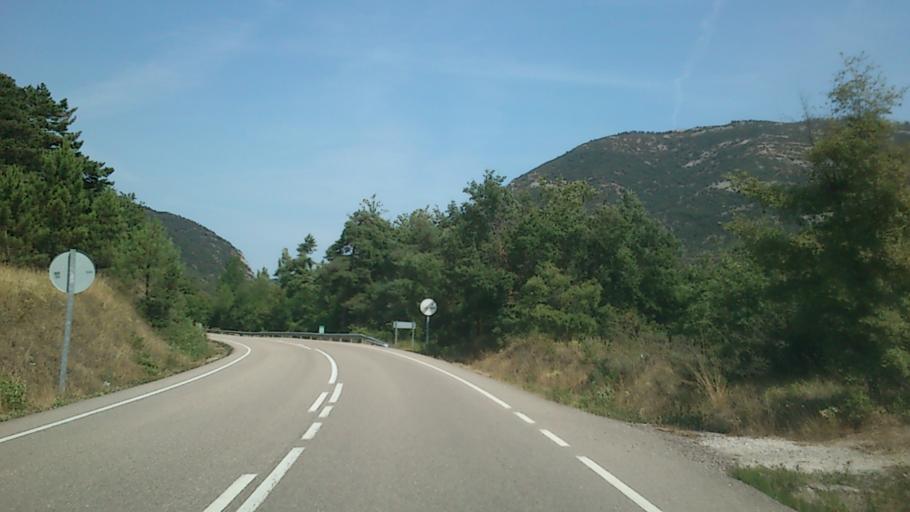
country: ES
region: Castille and Leon
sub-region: Provincia de Burgos
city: Trespaderne
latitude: 42.8793
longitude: -3.3261
